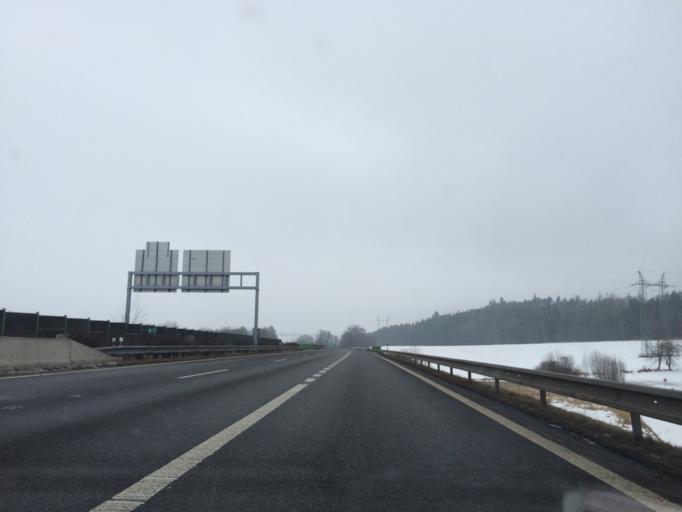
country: CZ
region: Jihocesky
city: Mirotice
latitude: 49.3552
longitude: 14.0552
